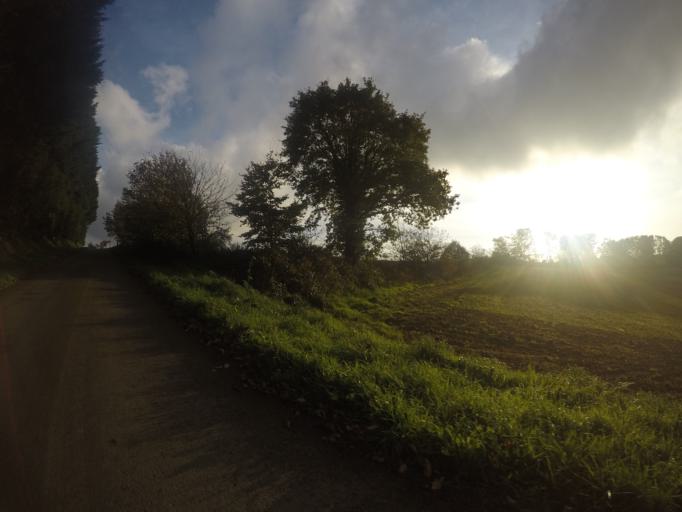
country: FR
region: Brittany
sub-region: Departement des Cotes-d'Armor
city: Bourbriac
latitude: 48.4638
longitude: -3.2905
